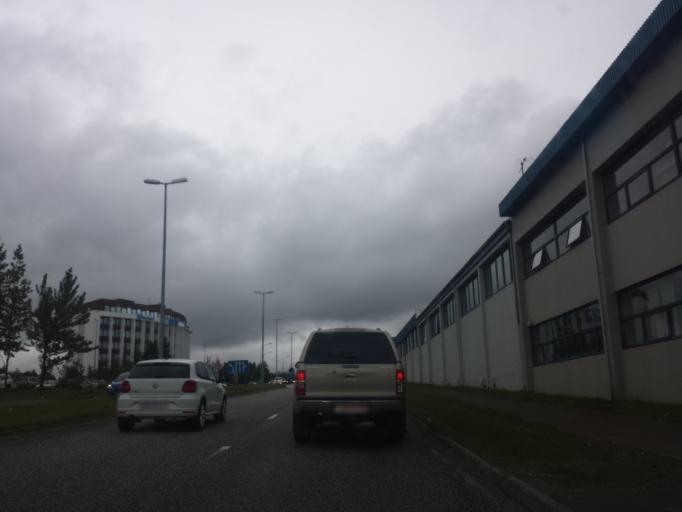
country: IS
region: Capital Region
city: Reykjavik
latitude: 64.1270
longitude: -21.8122
